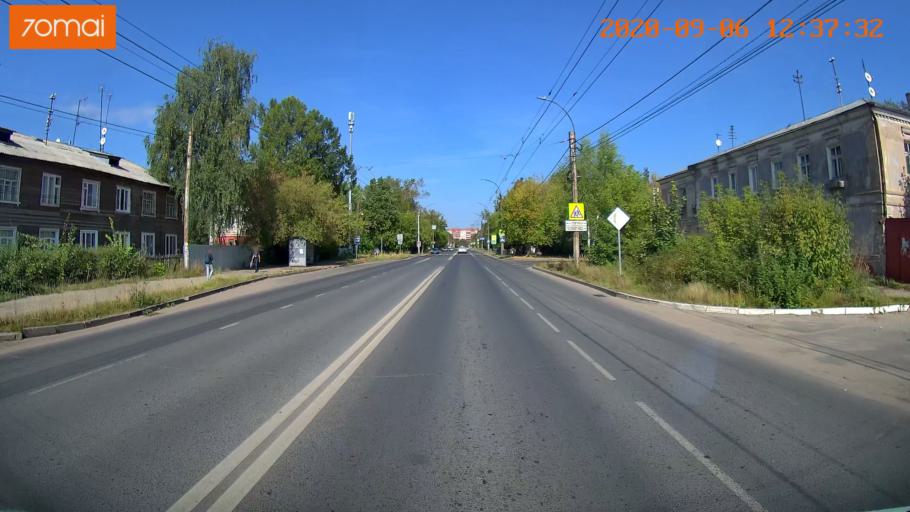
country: RU
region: Ivanovo
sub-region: Gorod Ivanovo
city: Ivanovo
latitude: 57.0277
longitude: 40.9801
